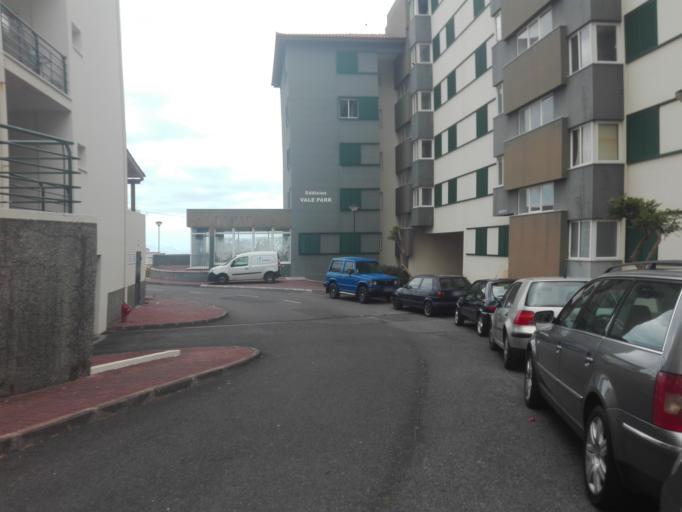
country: PT
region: Madeira
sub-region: Santa Cruz
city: Camacha
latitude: 32.6554
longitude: -16.8275
